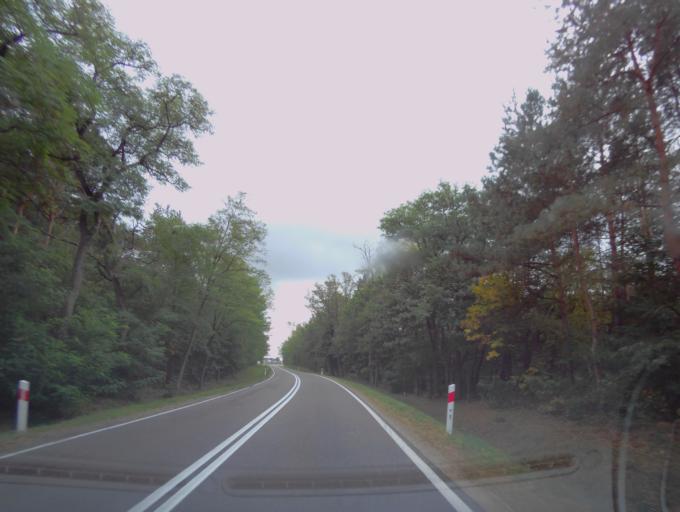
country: PL
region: Subcarpathian Voivodeship
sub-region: Powiat nizanski
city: Krzeszow
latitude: 50.3756
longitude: 22.3120
